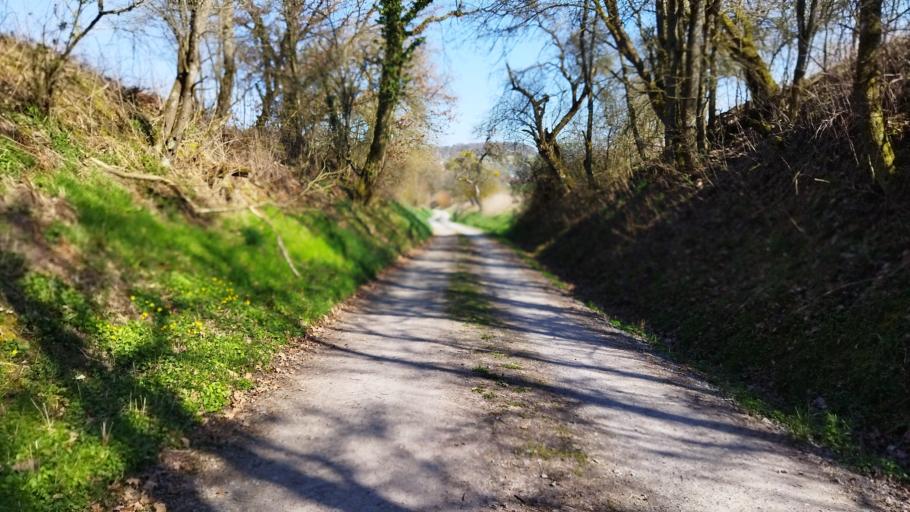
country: DE
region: Baden-Wuerttemberg
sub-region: Regierungsbezirk Stuttgart
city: Zaberfeld
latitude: 49.0248
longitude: 8.9117
